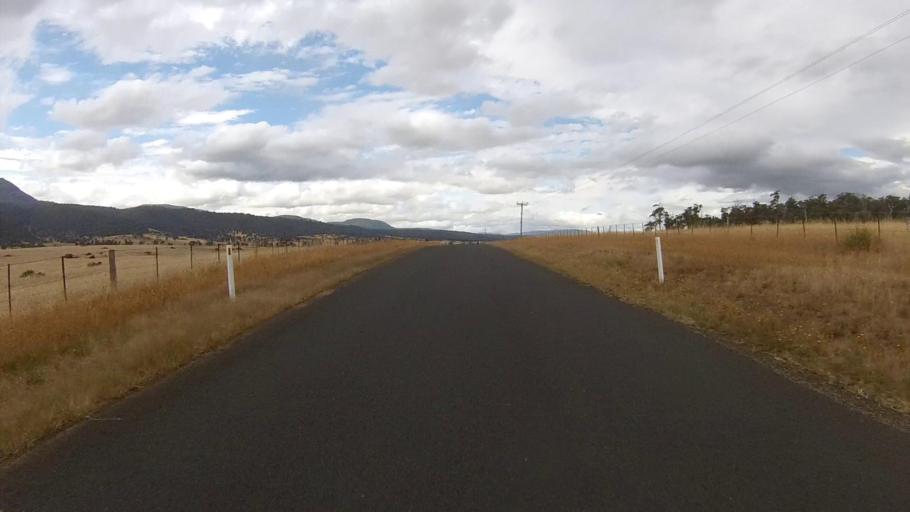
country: AU
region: Tasmania
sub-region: Northern Midlands
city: Evandale
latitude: -41.8249
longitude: 147.8078
